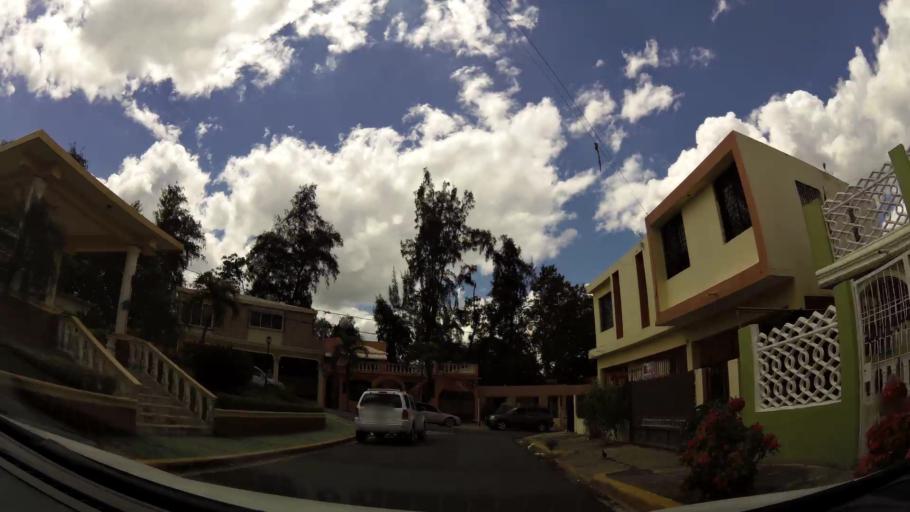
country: DO
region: Nacional
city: Ensanche Luperon
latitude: 18.5167
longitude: -69.9091
